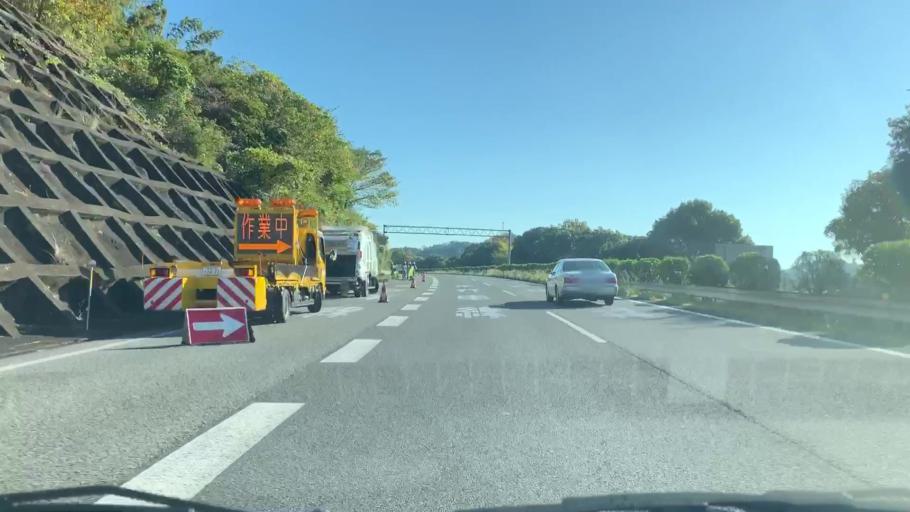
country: JP
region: Saga Prefecture
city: Saga-shi
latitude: 33.2866
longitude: 130.1543
